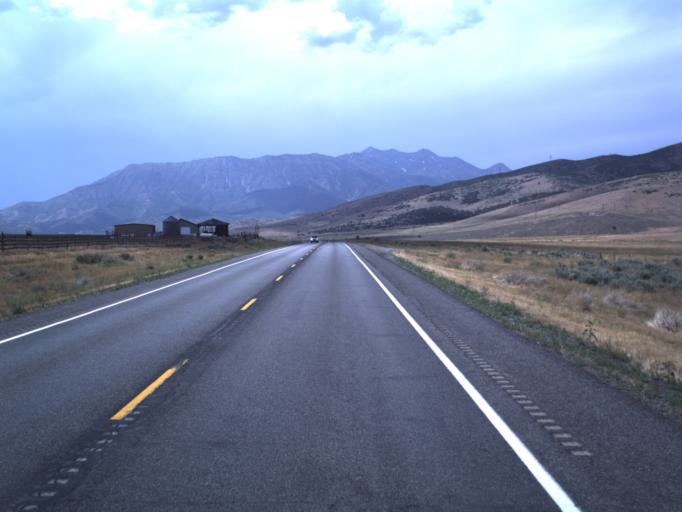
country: US
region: Utah
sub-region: Sanpete County
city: Fountain Green
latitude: 39.6752
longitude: -111.6669
